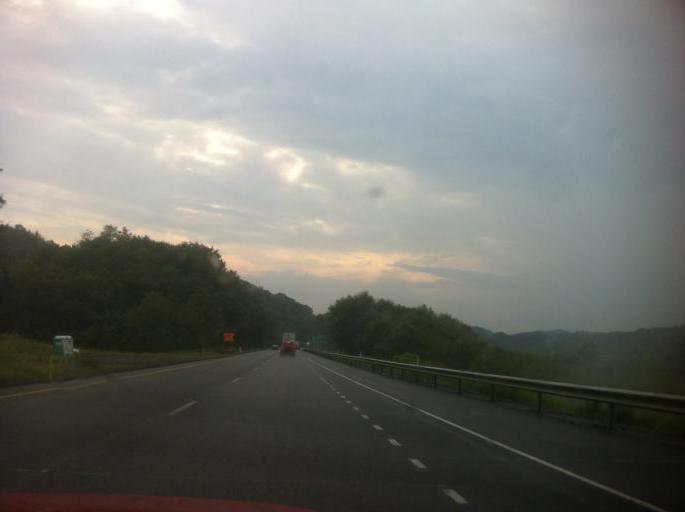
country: US
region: Pennsylvania
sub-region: Clarion County
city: Clarion
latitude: 41.1863
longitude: -79.4031
